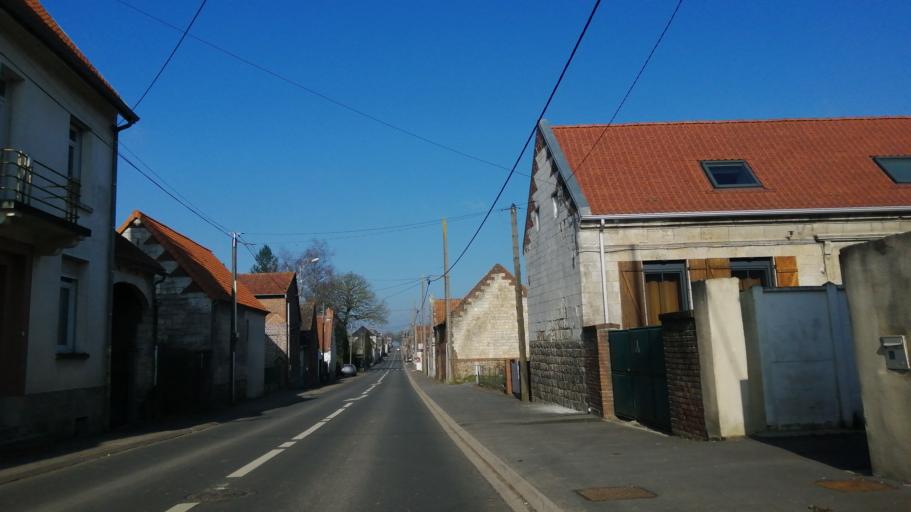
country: FR
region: Nord-Pas-de-Calais
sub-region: Departement du Pas-de-Calais
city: Aubigny-en-Artois
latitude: 50.3953
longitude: 2.6128
